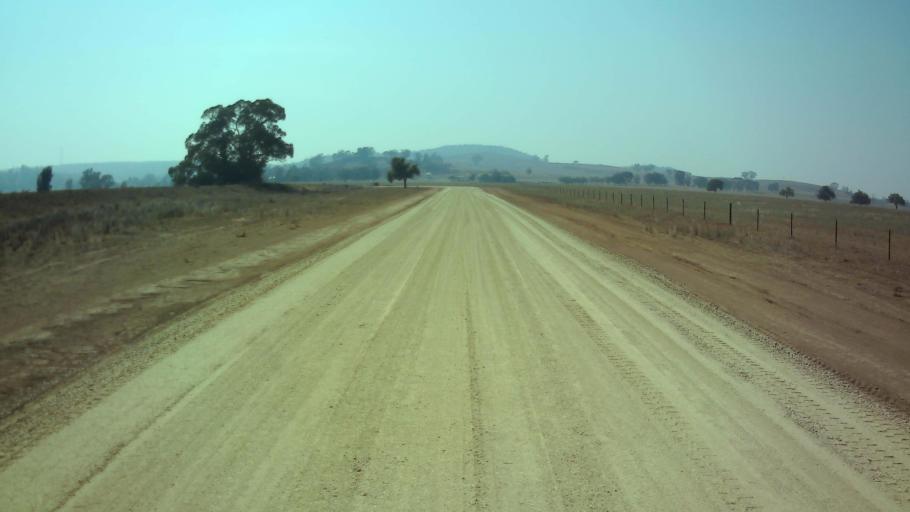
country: AU
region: New South Wales
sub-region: Weddin
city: Grenfell
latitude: -33.8570
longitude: 148.1091
